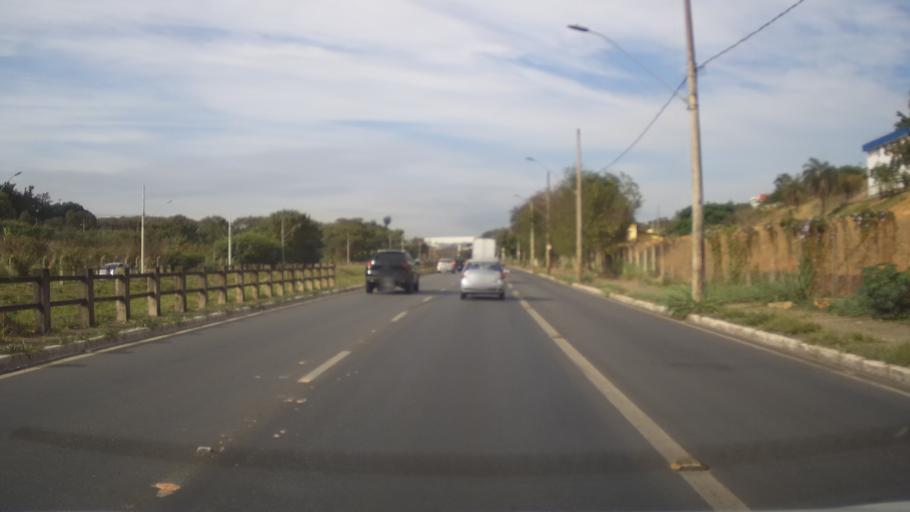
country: BR
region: Minas Gerais
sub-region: Contagem
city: Contagem
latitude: -19.8934
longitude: -44.0404
